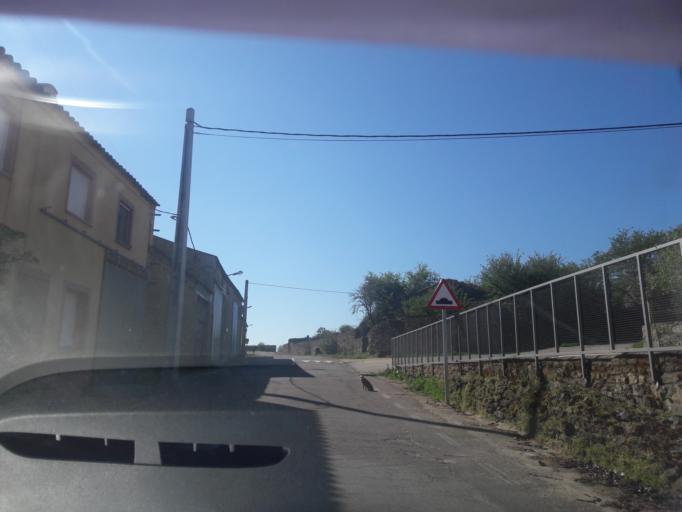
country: ES
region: Castille and Leon
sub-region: Provincia de Salamanca
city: Valsalabroso
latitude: 41.1523
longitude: -6.4876
